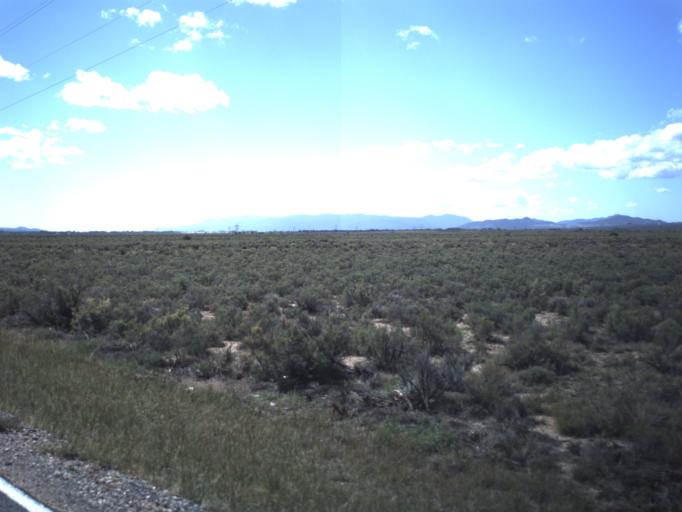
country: US
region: Utah
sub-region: Iron County
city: Enoch
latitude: 37.8230
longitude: -113.0504
